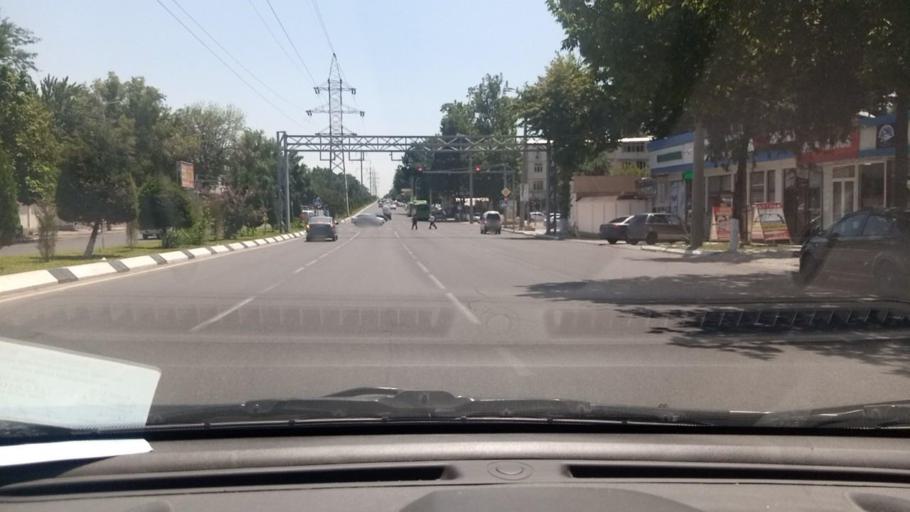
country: UZ
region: Toshkent Shahri
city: Tashkent
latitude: 41.2986
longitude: 69.1939
